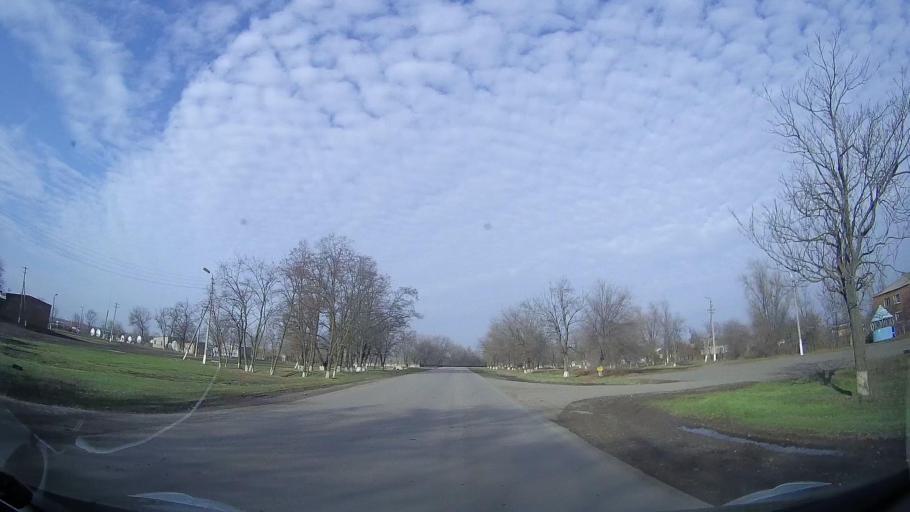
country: RU
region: Rostov
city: Gigant
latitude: 46.8379
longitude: 41.3322
